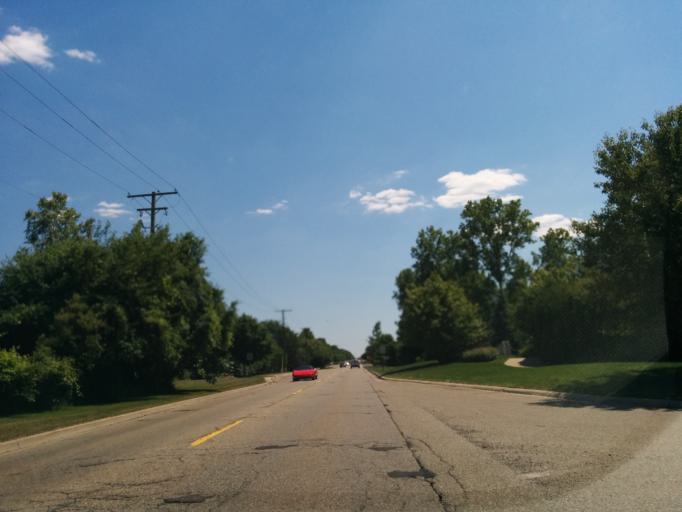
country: US
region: Michigan
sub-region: Oakland County
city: West Bloomfield Township
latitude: 42.5352
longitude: -83.3800
